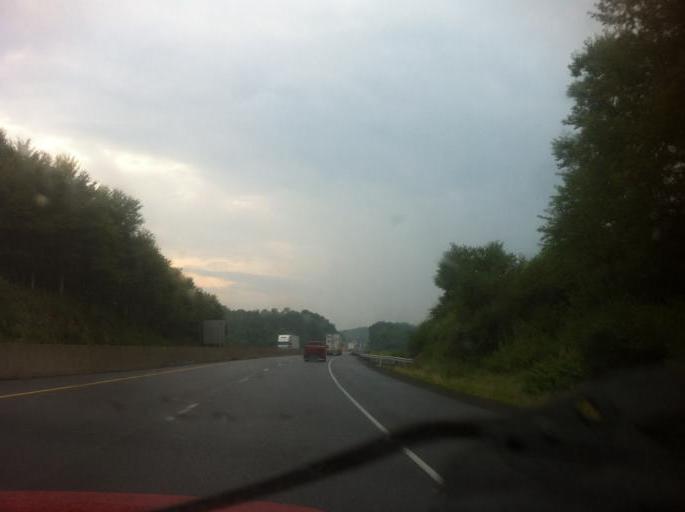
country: US
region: Pennsylvania
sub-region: Clarion County
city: Clarion
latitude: 41.1869
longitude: -79.4105
